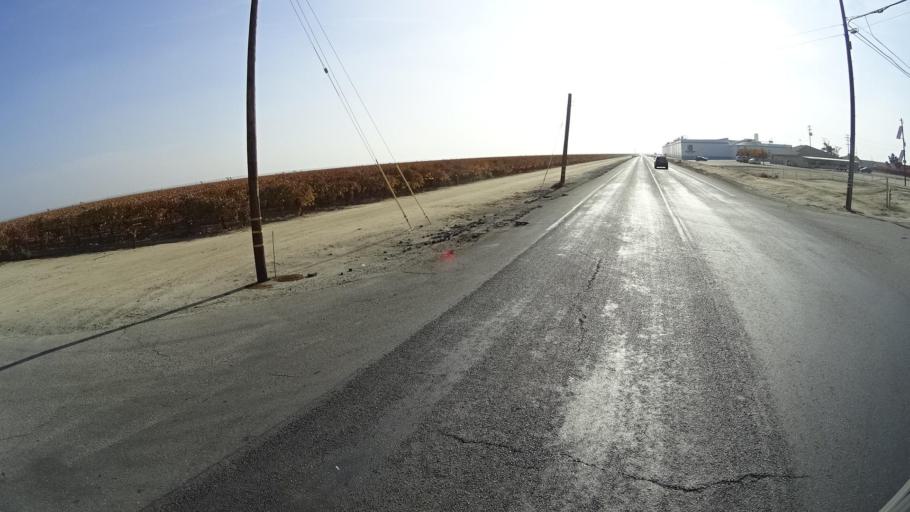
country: US
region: California
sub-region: Tulare County
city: Richgrove
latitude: 35.7762
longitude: -119.1236
